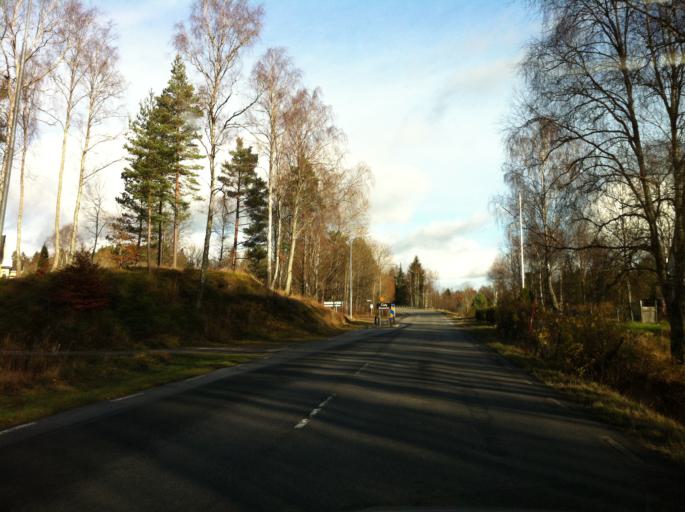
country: SE
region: Kronoberg
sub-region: Almhults Kommun
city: AElmhult
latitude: 56.4744
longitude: 14.0929
